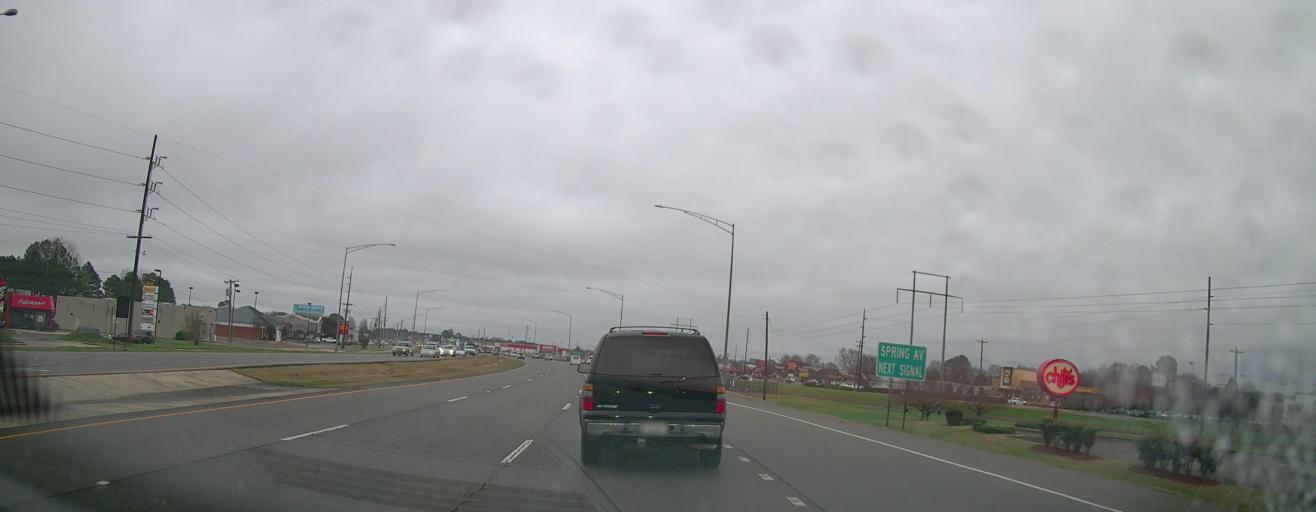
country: US
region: Alabama
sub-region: Morgan County
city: Decatur
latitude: 34.5605
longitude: -87.0048
